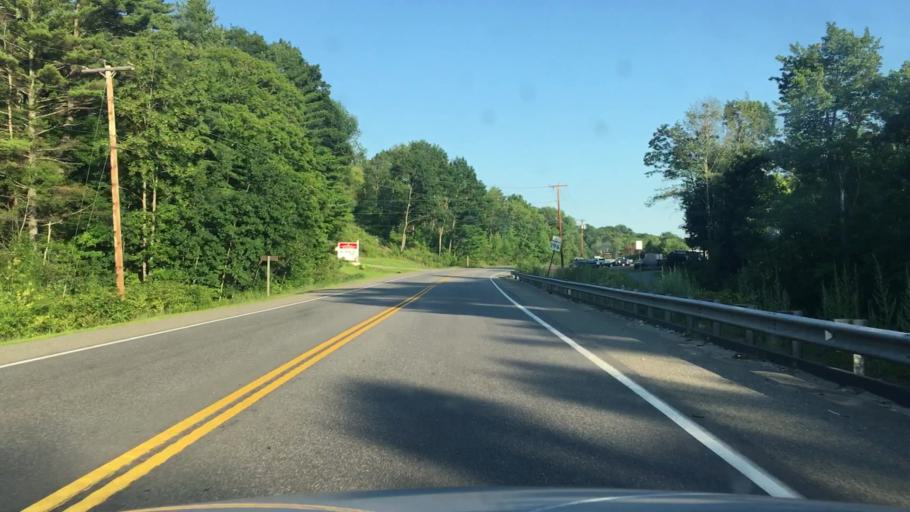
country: US
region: Maine
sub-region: Androscoggin County
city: Lisbon
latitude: 44.0110
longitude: -70.0859
